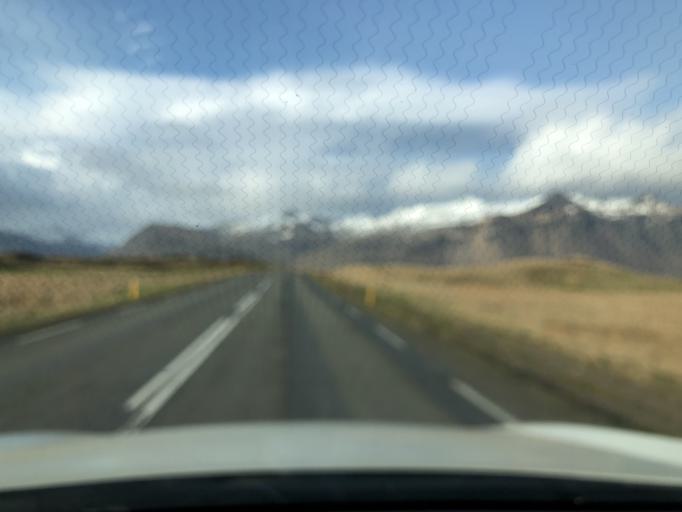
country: IS
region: East
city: Hoefn
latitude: 64.2801
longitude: -15.1934
